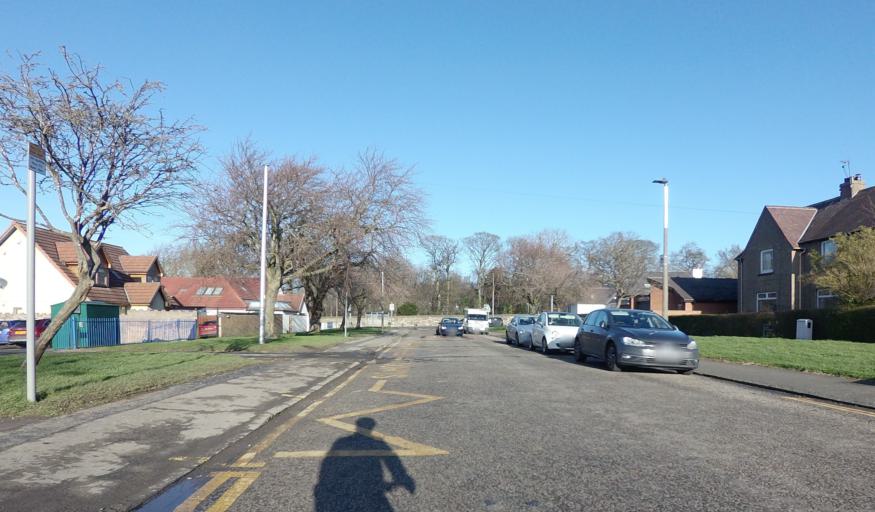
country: GB
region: Scotland
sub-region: Edinburgh
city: Colinton
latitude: 55.9604
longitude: -3.2896
